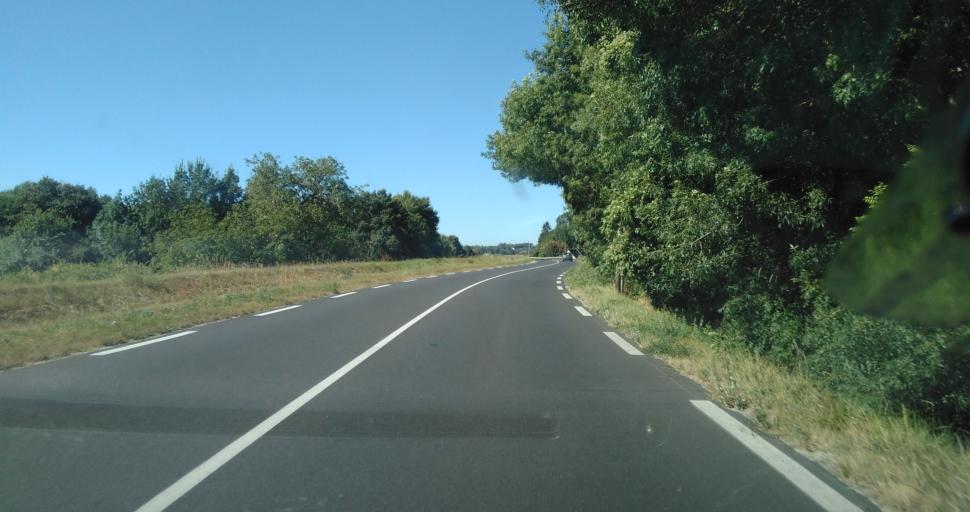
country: FR
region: Centre
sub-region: Departement d'Indre-et-Loire
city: Nazelles-Negron
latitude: 47.4105
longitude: 0.9523
